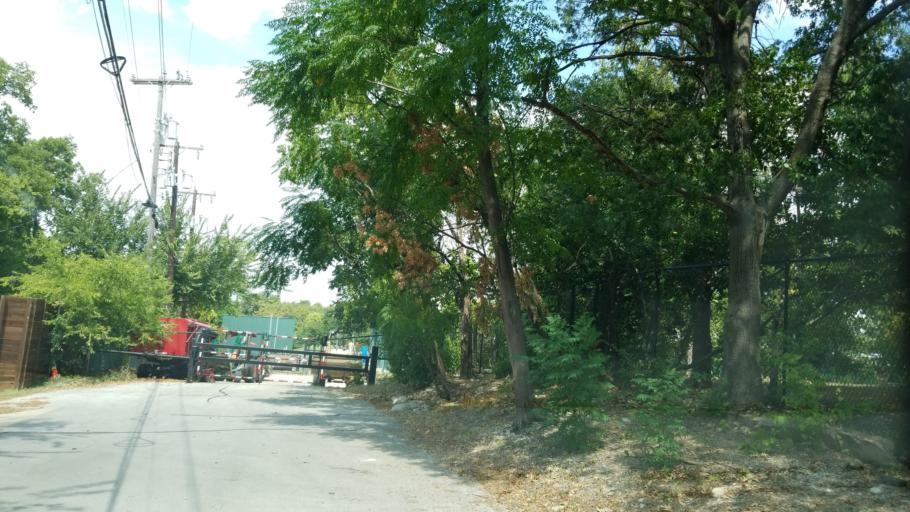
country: US
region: Texas
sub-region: Dallas County
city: Cockrell Hill
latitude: 32.7550
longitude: -96.8481
